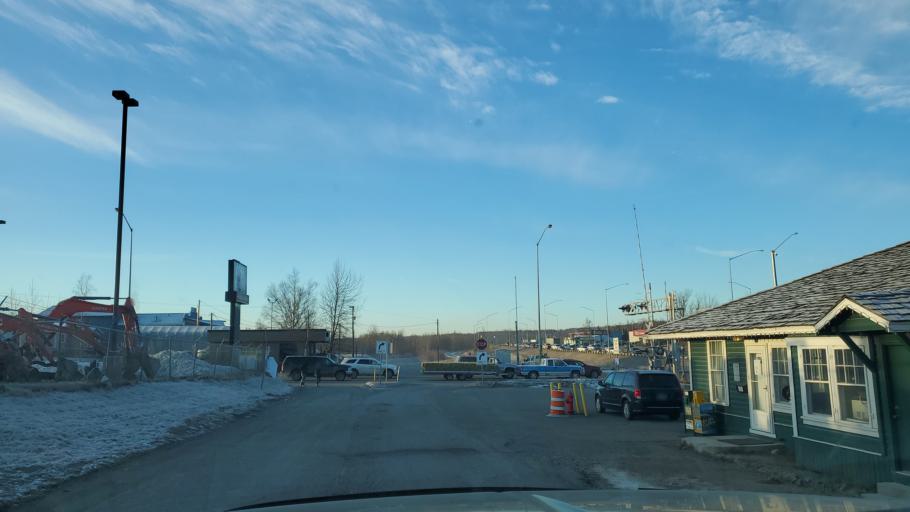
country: US
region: Alaska
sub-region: Matanuska-Susitna Borough
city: Wasilla
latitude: 61.5803
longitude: -149.4403
